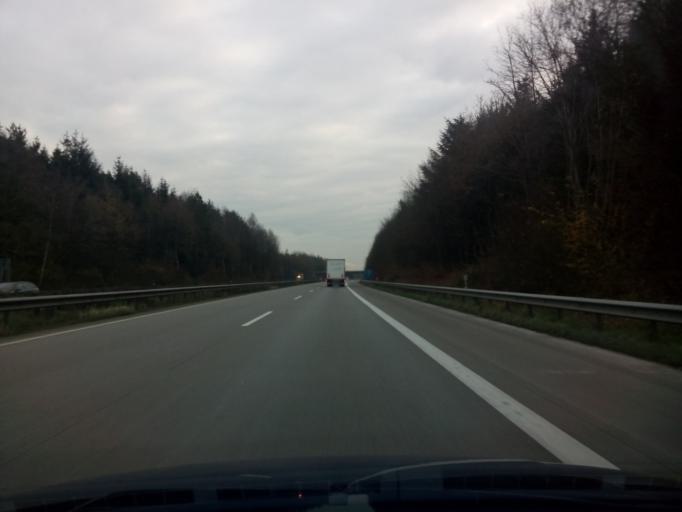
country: DE
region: Lower Saxony
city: Langen
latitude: 53.6147
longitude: 8.6624
